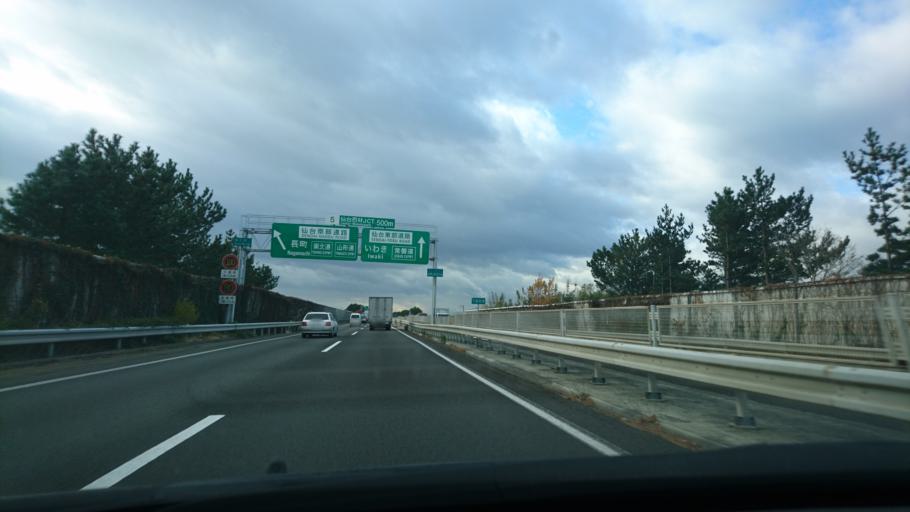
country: JP
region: Miyagi
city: Sendai
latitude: 38.2150
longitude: 140.9478
